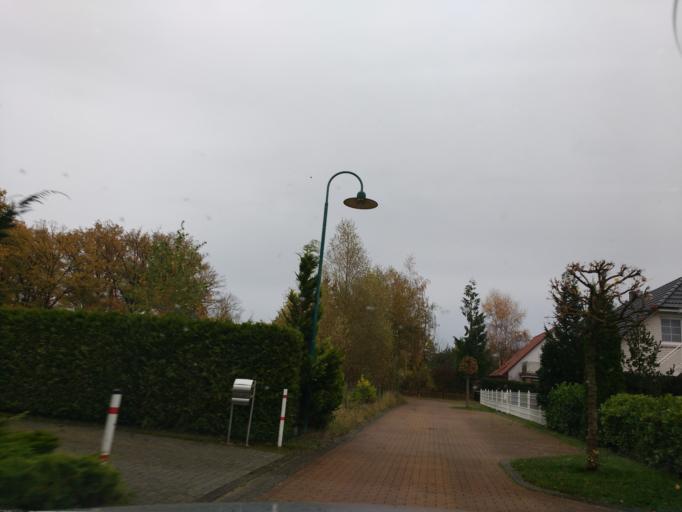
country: DE
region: Mecklenburg-Vorpommern
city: Ostseebad Boltenhagen
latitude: 53.9792
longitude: 11.2390
